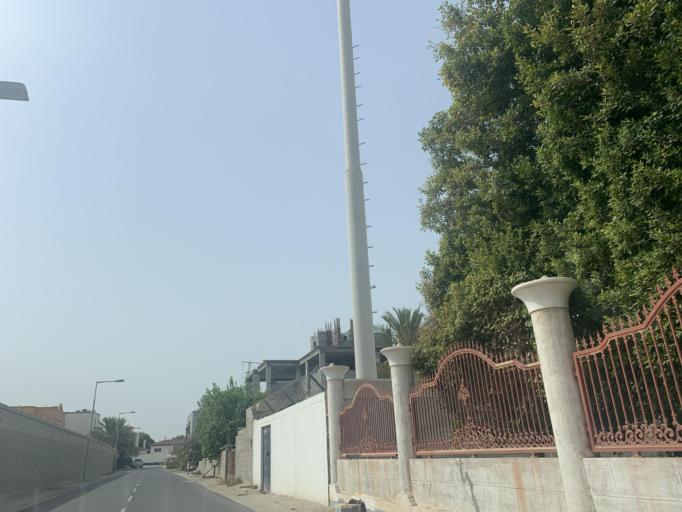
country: BH
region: Manama
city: Jidd Hafs
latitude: 26.1996
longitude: 50.4818
